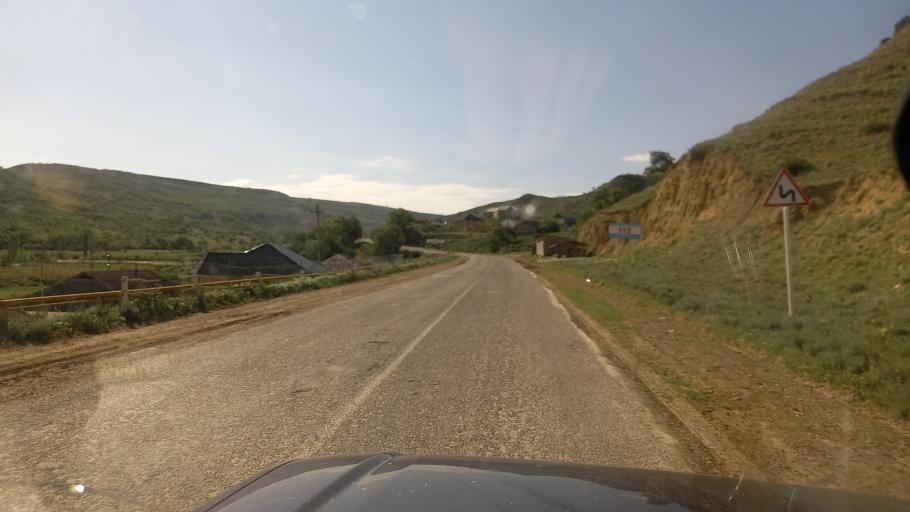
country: RU
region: Dagestan
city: Syrtych
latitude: 41.9470
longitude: 48.1589
